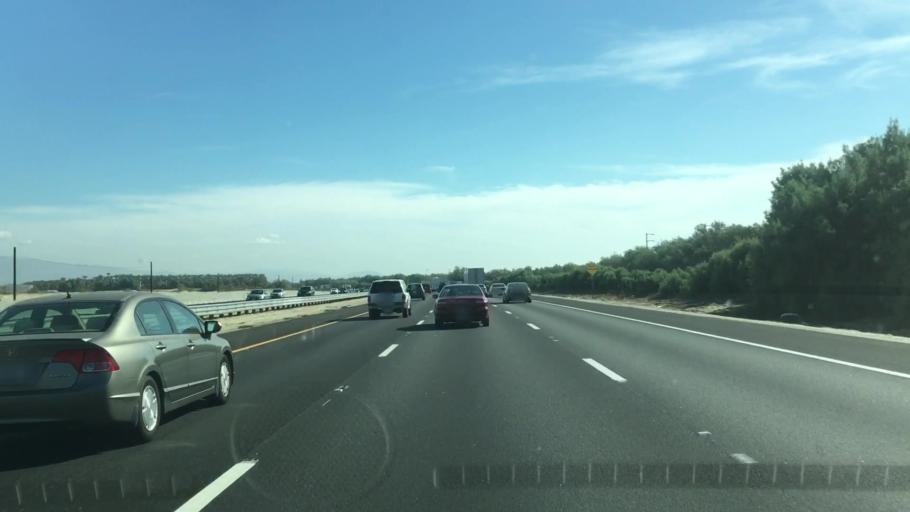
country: US
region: California
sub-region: Riverside County
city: Bermuda Dunes
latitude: 33.7671
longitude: -116.3237
